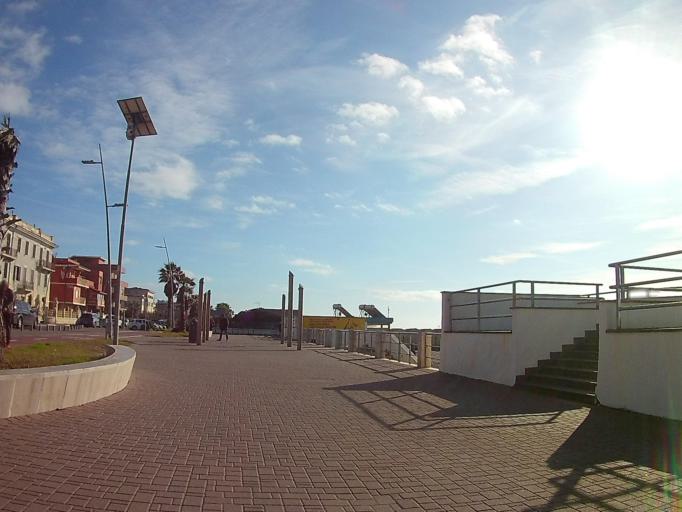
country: IT
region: Latium
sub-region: Citta metropolitana di Roma Capitale
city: Lido di Ostia
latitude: 41.7337
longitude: 12.2635
